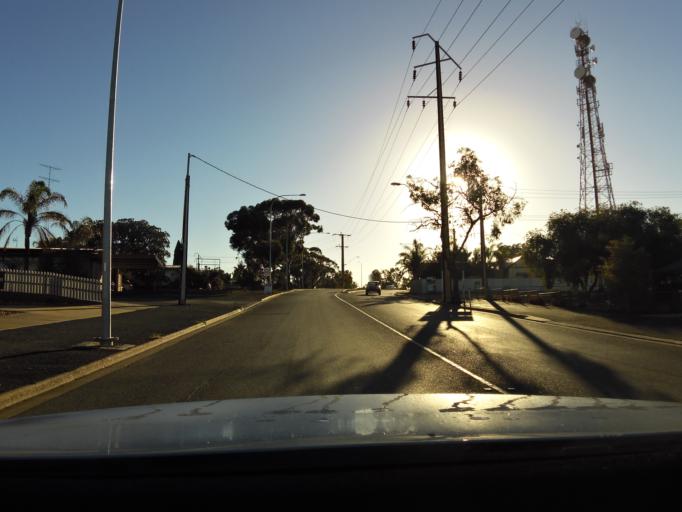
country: AU
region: South Australia
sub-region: Berri and Barmera
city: Berri
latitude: -34.2829
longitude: 140.5968
